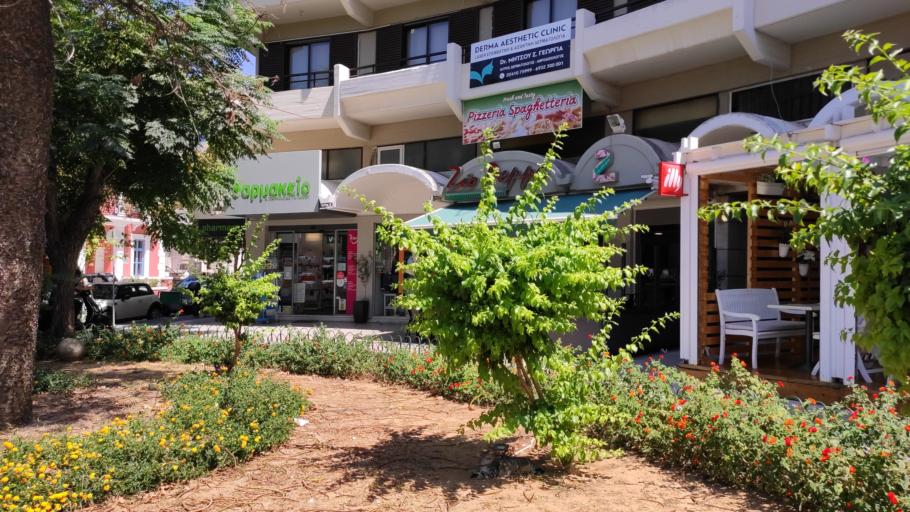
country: GR
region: South Aegean
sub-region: Nomos Dodekanisou
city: Rodos
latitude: 36.4498
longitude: 28.2217
